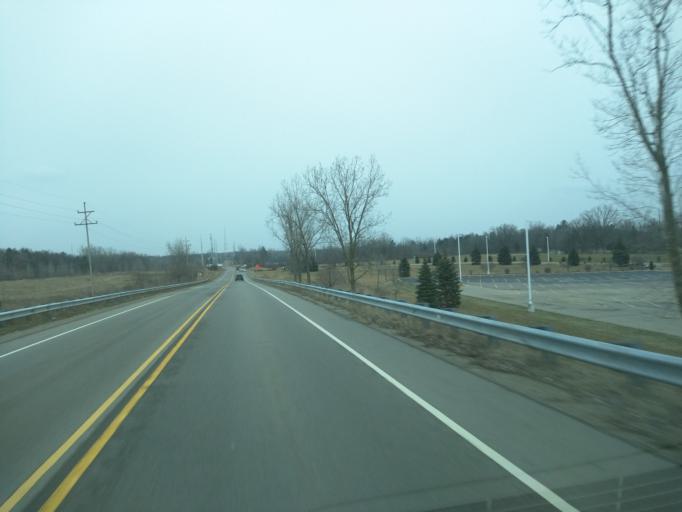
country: US
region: Michigan
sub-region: Eaton County
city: Waverly
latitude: 42.7185
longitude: -84.6229
